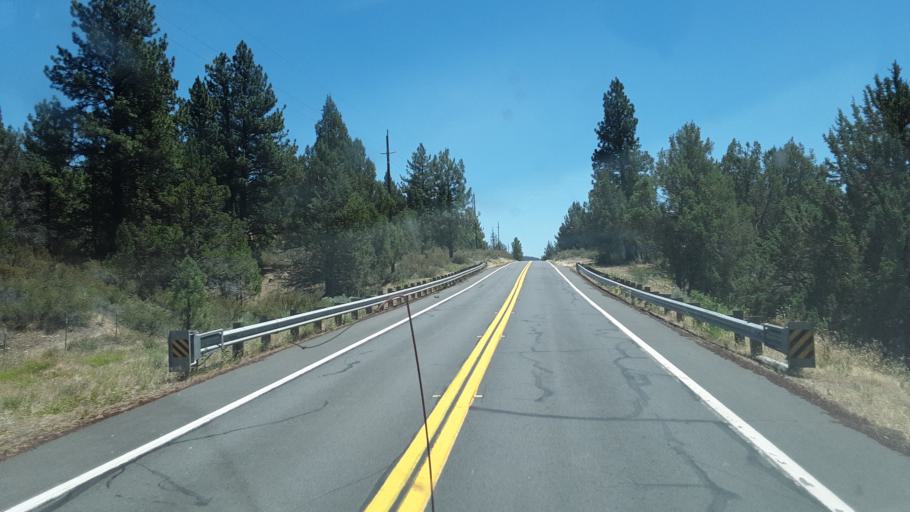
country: US
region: California
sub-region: Modoc County
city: Alturas
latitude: 41.0713
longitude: -120.8865
